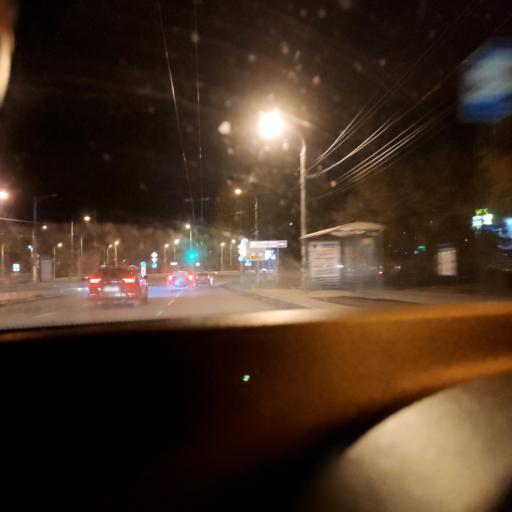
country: RU
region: Samara
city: Samara
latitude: 53.2149
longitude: 50.1879
